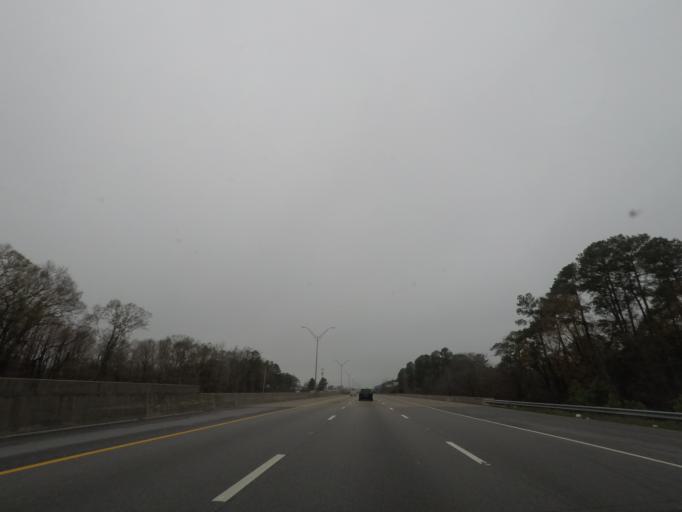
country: US
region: North Carolina
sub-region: Robeson County
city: Lumberton
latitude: 34.6327
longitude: -79.0289
